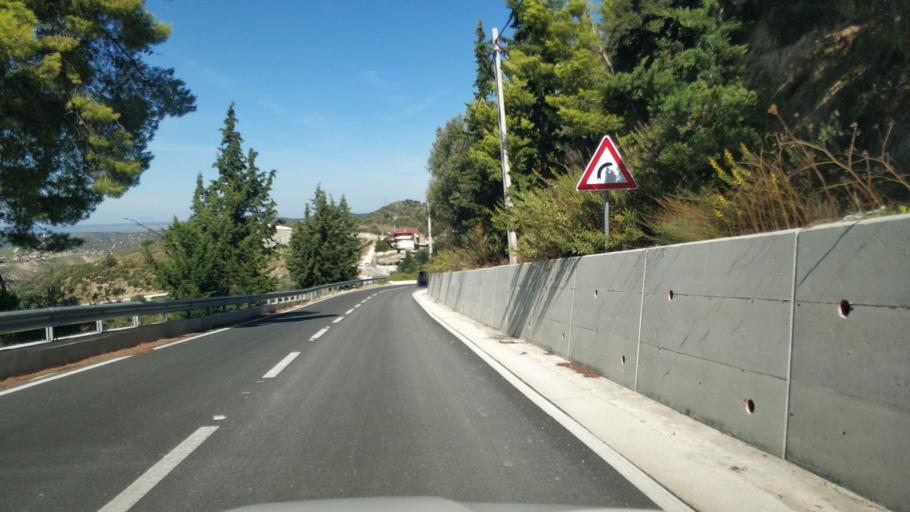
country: AL
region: Vlore
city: Vlore
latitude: 40.4527
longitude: 19.5151
